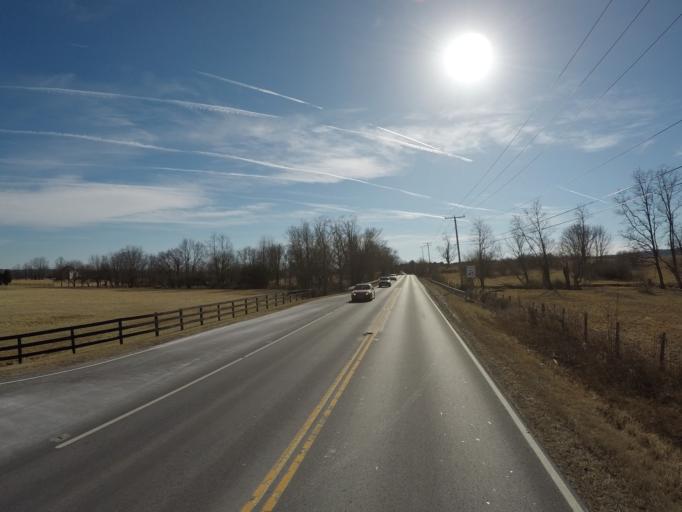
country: US
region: Maryland
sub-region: Frederick County
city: Point of Rocks
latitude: 39.2013
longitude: -77.5377
